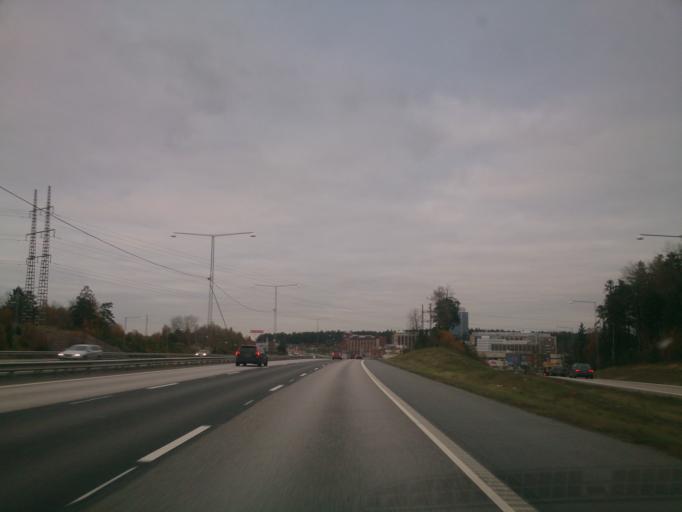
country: SE
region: Stockholm
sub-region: Upplands Vasby Kommun
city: Upplands Vaesby
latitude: 59.4926
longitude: 17.9209
